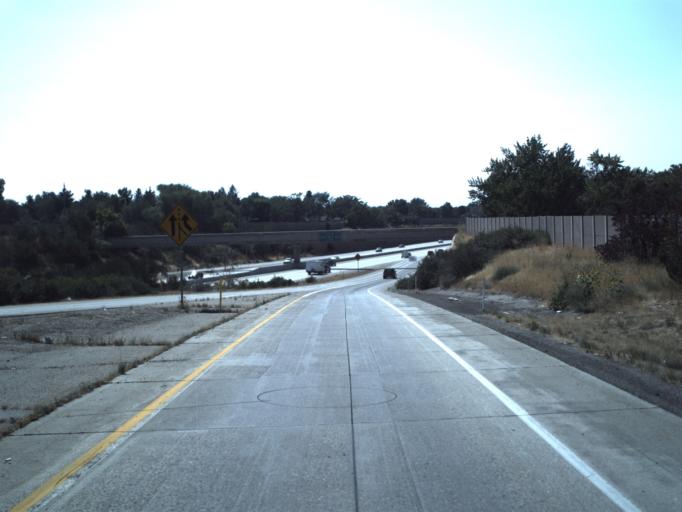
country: US
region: Utah
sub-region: Salt Lake County
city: Cottonwood Heights
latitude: 40.6333
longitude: -111.8359
